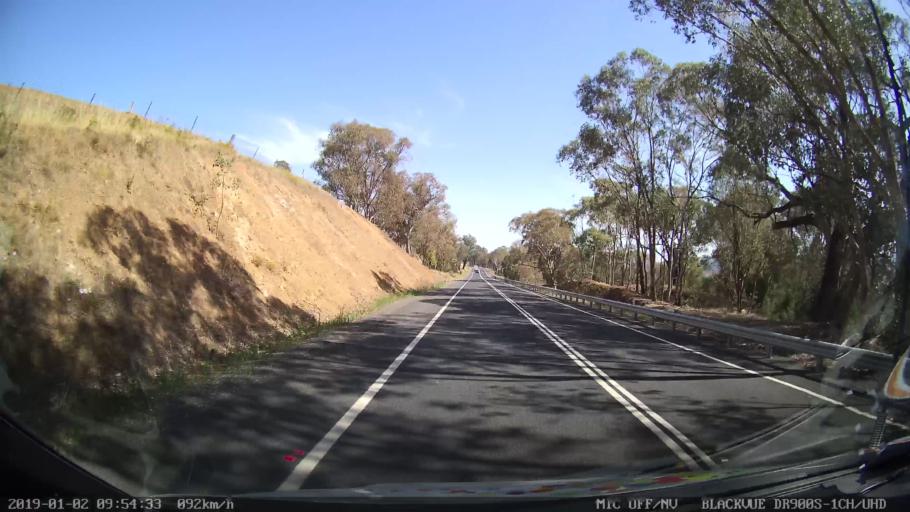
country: AU
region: New South Wales
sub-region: Tumut Shire
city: Tumut
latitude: -35.2338
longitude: 148.1958
